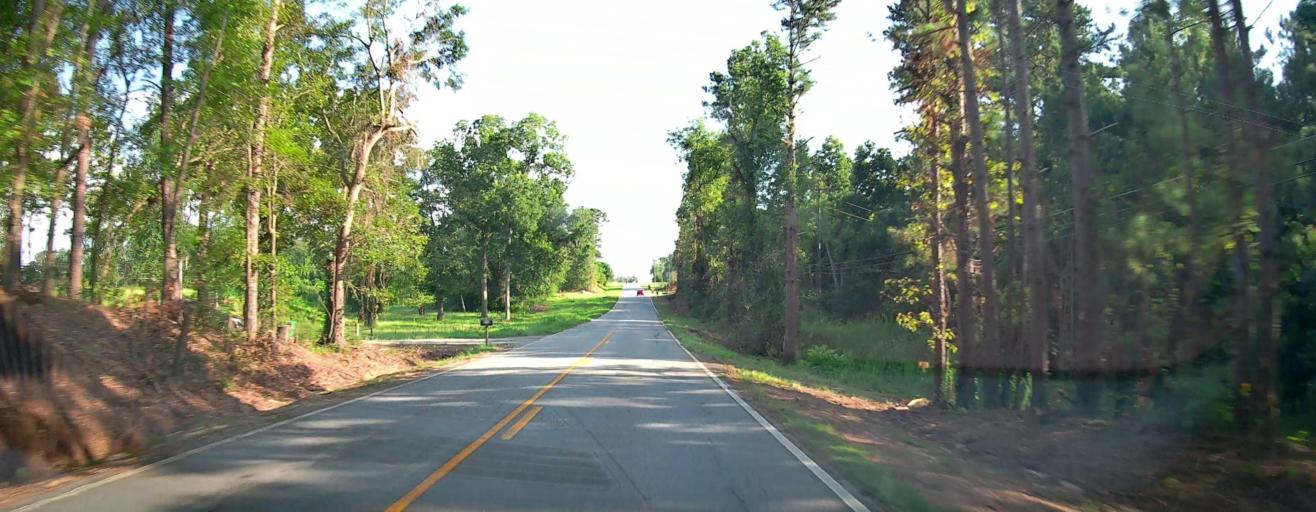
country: US
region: Georgia
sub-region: Houston County
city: Robins Air Force Base
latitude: 32.5566
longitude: -83.6045
